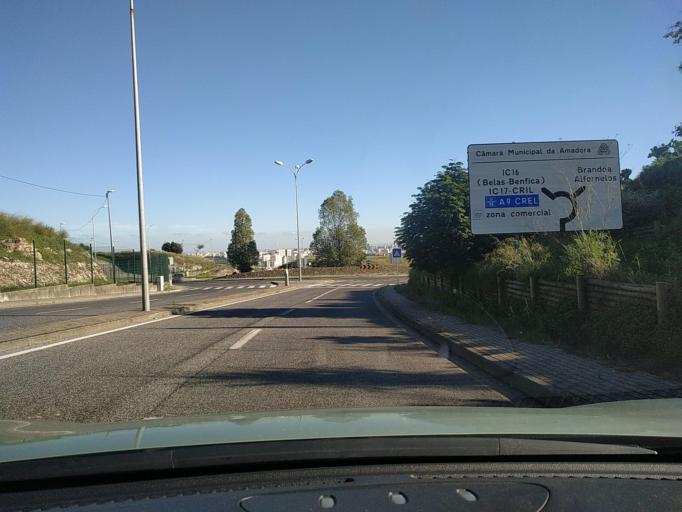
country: PT
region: Lisbon
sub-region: Amadora
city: Amadora
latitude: 38.7720
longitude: -9.2261
